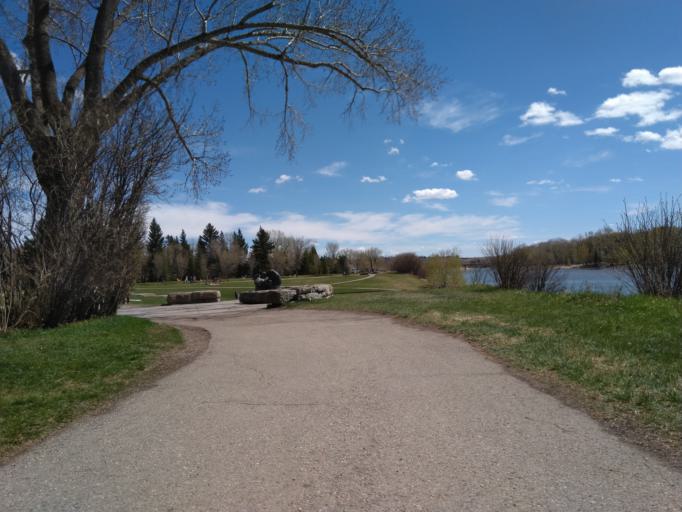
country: CA
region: Alberta
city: Calgary
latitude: 51.0998
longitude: -114.2203
